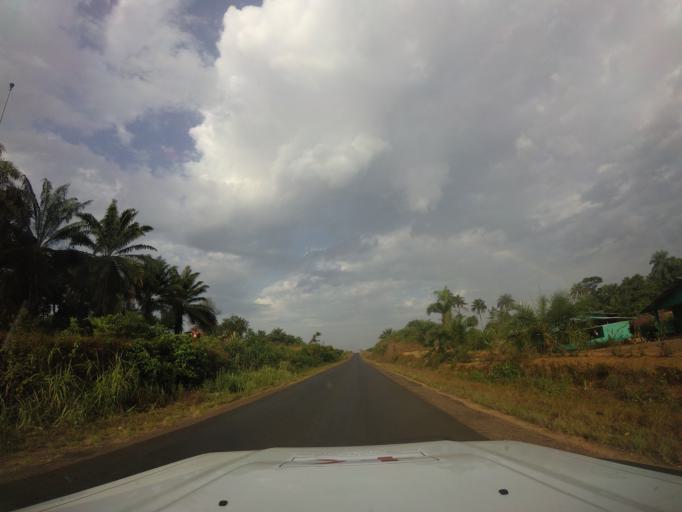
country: LR
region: Bomi
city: Tubmanburg
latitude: 6.7289
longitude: -11.0239
